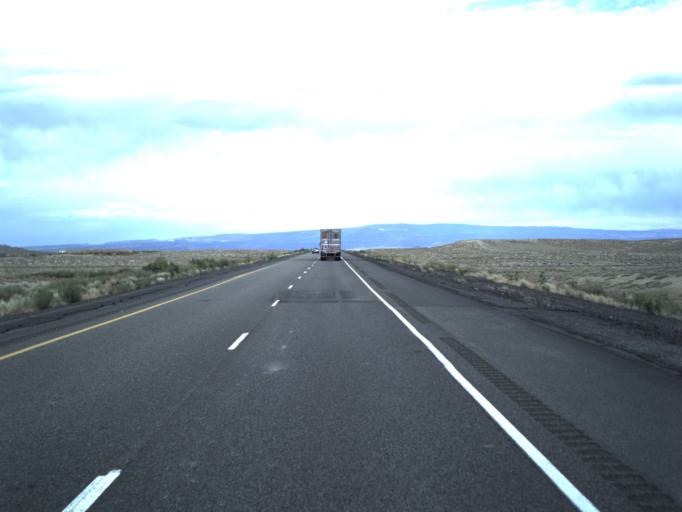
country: US
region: Utah
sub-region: Grand County
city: Moab
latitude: 38.9388
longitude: -109.5021
